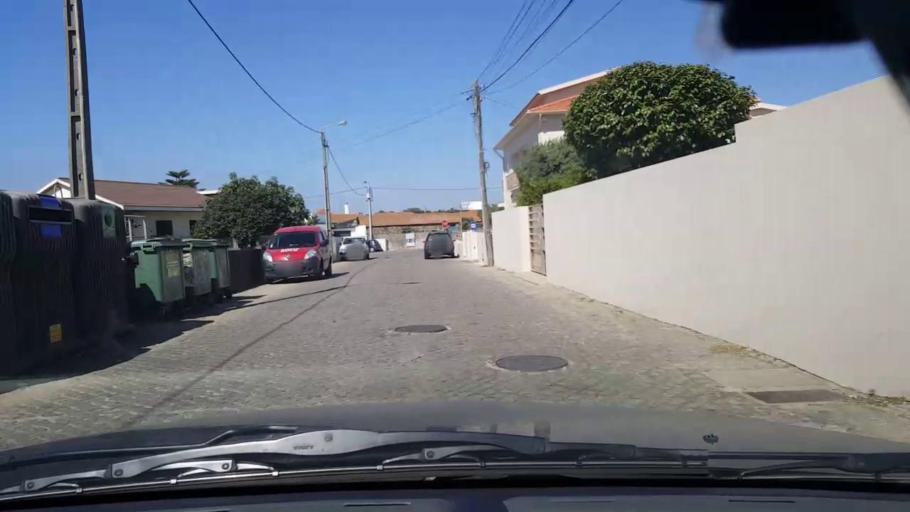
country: PT
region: Porto
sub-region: Matosinhos
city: Lavra
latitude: 41.2917
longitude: -8.7262
